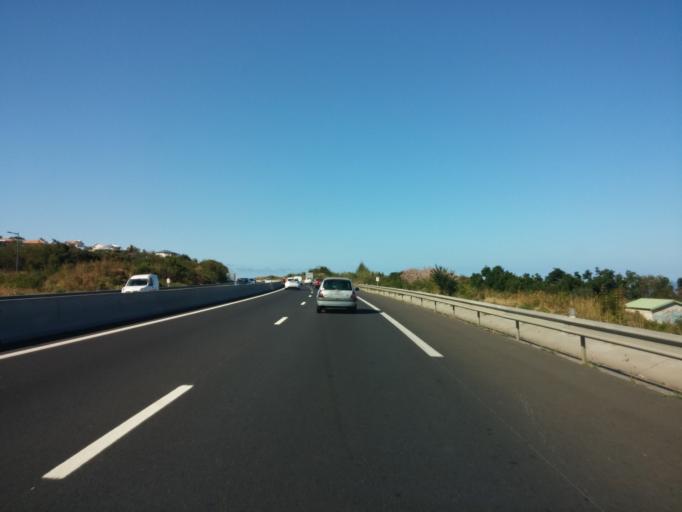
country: RE
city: Piton Saint-Leu
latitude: -21.2062
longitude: 55.2924
